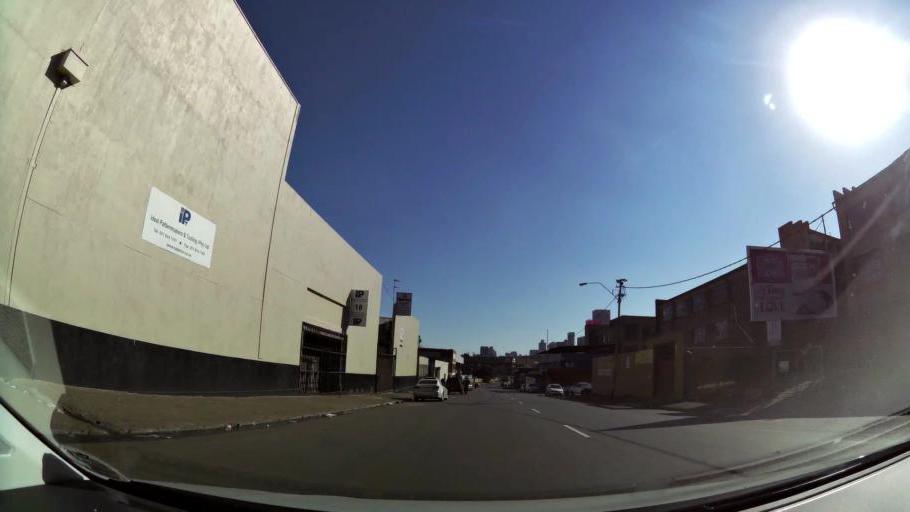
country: ZA
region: Gauteng
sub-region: City of Johannesburg Metropolitan Municipality
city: Johannesburg
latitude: -26.2090
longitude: 28.0631
